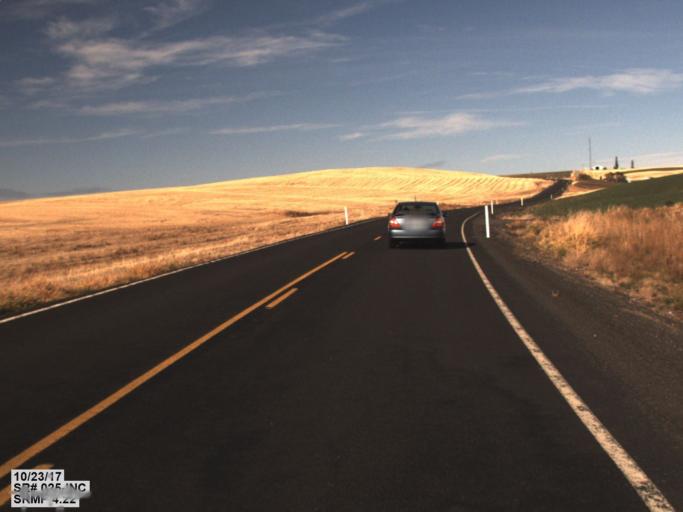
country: US
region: Washington
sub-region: Lincoln County
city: Davenport
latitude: 47.7135
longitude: -118.1514
